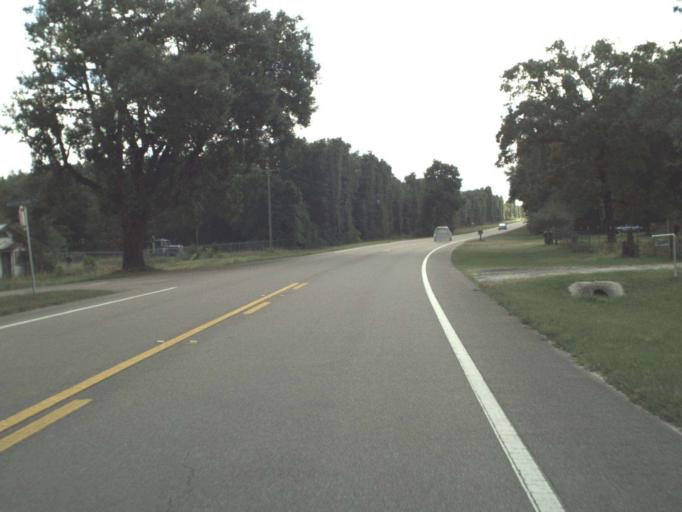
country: US
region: Florida
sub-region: Walton County
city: Freeport
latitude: 30.5740
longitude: -85.9251
